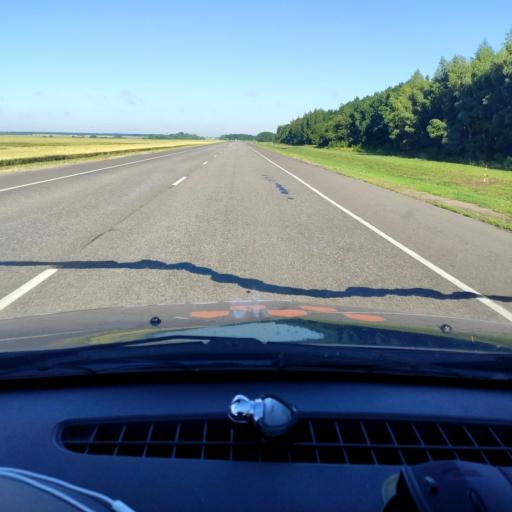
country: RU
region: Orjol
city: Pokrovskoye
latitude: 52.6231
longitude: 36.8152
